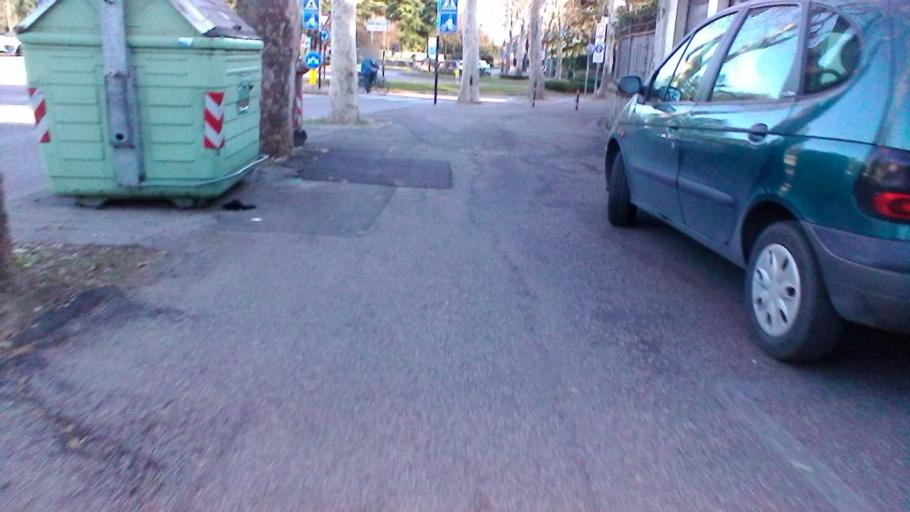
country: IT
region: Veneto
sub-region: Provincia di Verona
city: Verona
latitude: 45.4355
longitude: 10.9785
